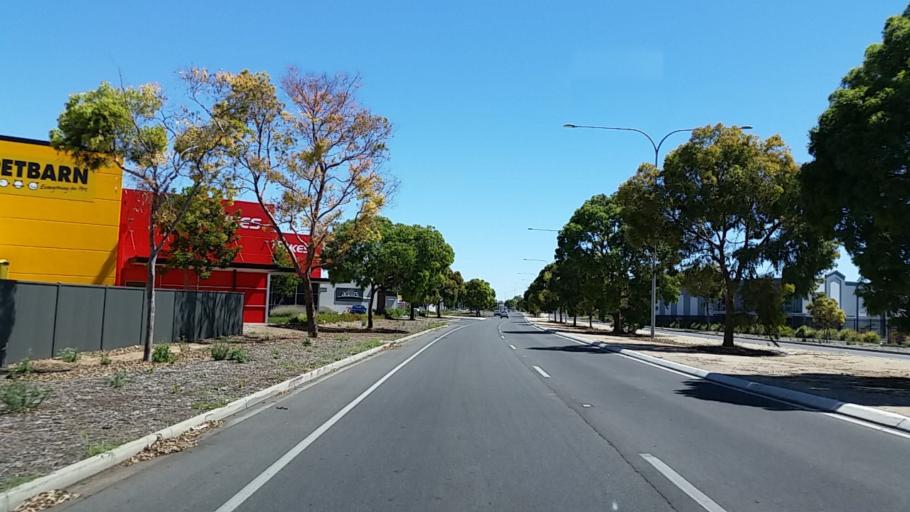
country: AU
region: South Australia
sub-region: Unley
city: Forestville
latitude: -34.9332
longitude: 138.5739
